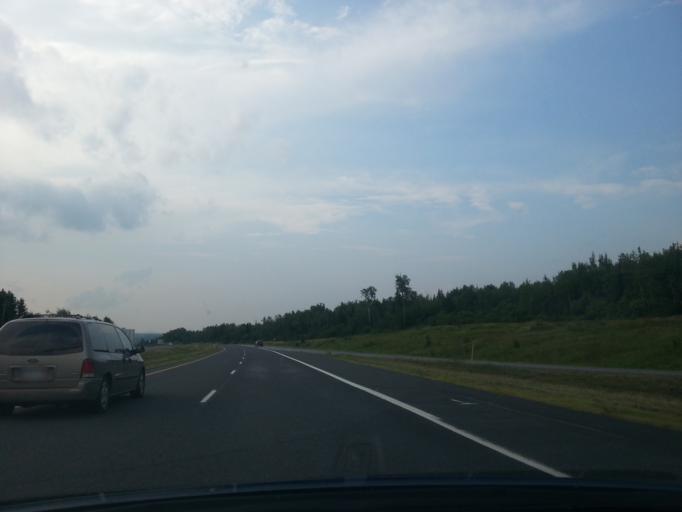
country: CA
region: New Brunswick
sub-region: Madawaska County
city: Saint-Leonard
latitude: 47.1731
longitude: -67.9172
